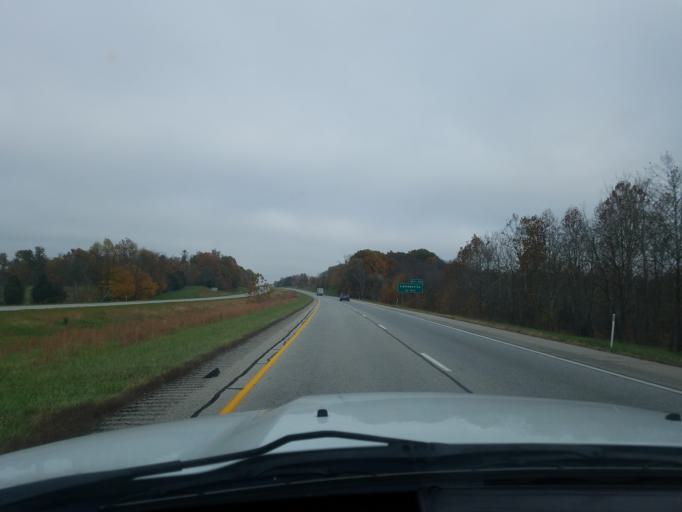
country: US
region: Indiana
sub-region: Floyd County
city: Georgetown
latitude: 38.2563
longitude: -86.0172
